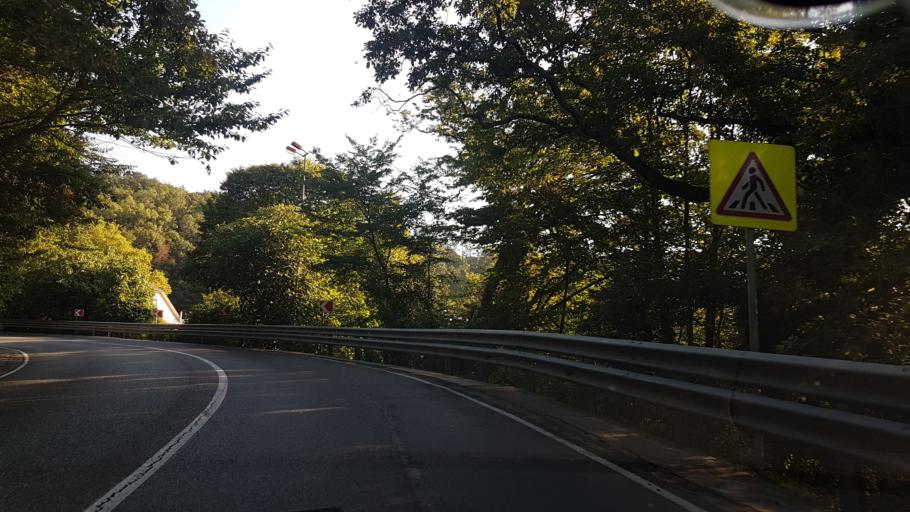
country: RU
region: Krasnodarskiy
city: Dagomys
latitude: 43.6559
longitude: 39.6452
